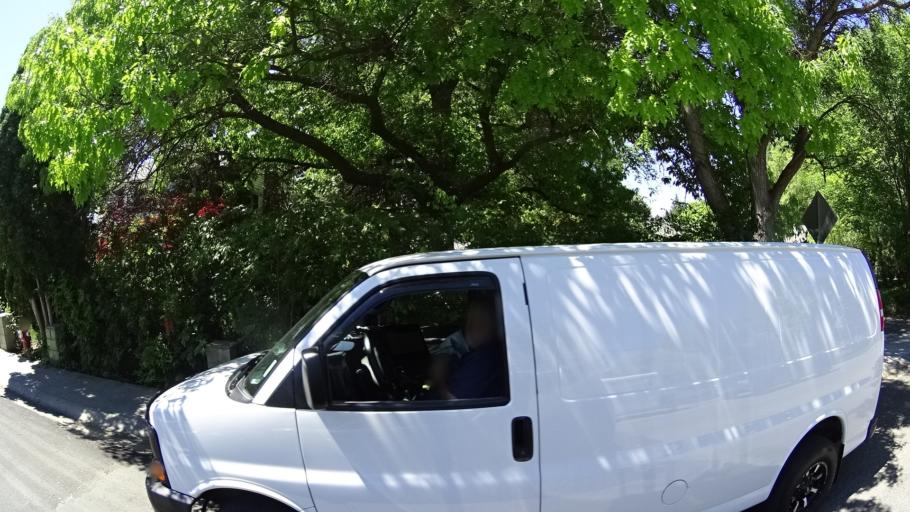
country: US
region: Idaho
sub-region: Ada County
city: Garden City
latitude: 43.5843
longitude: -116.2371
